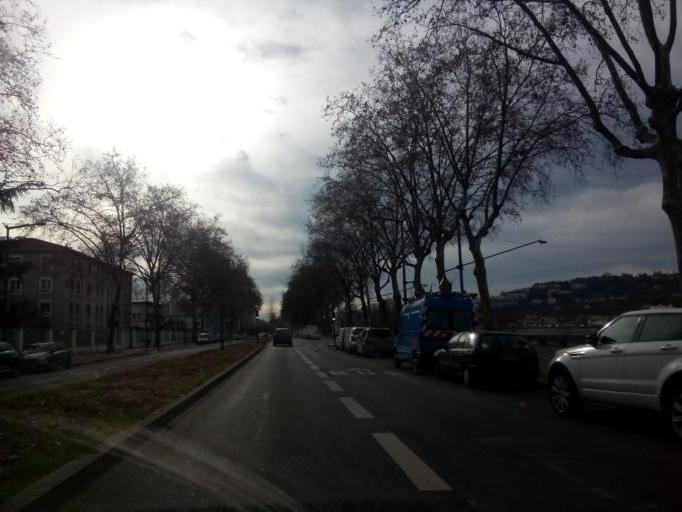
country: FR
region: Rhone-Alpes
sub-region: Departement du Rhone
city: Lyon
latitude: 45.7420
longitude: 4.8282
